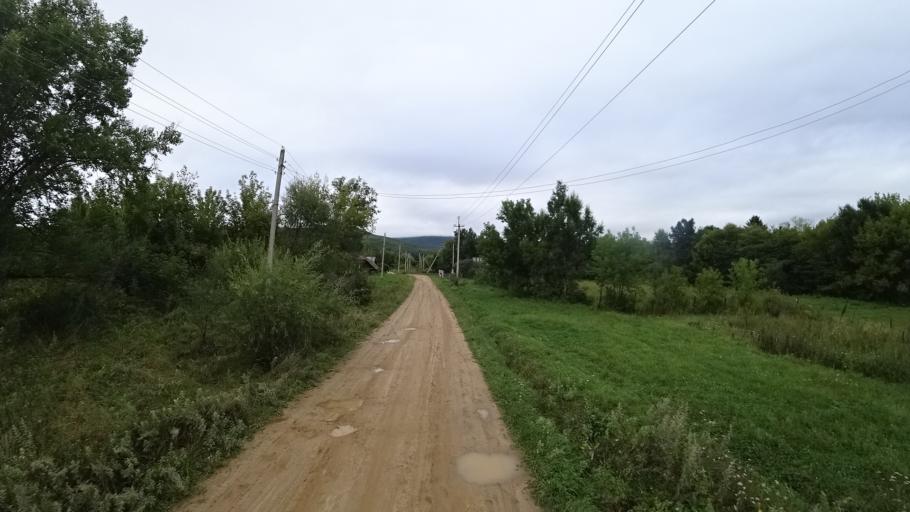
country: RU
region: Primorskiy
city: Rettikhovka
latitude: 44.1407
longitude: 132.6415
